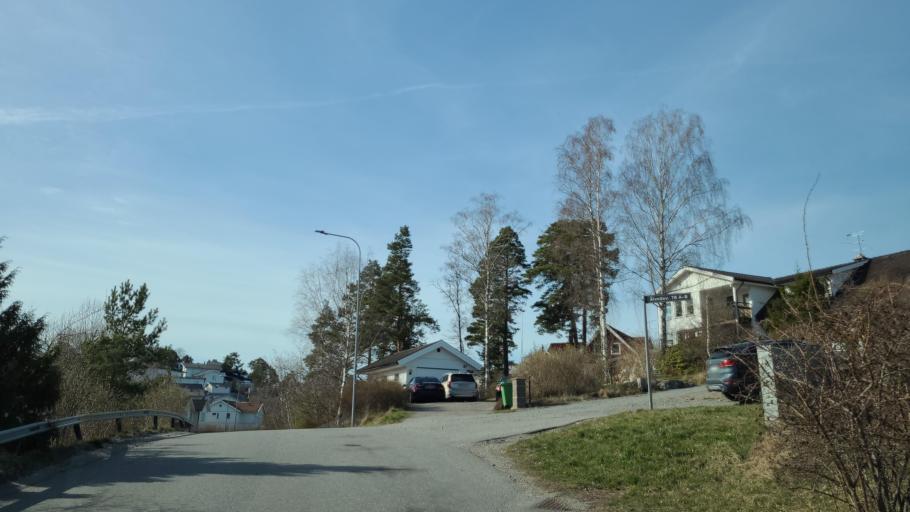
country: SE
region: Stockholm
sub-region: Ekero Kommun
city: Ekeroe
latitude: 59.2879
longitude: 17.7665
